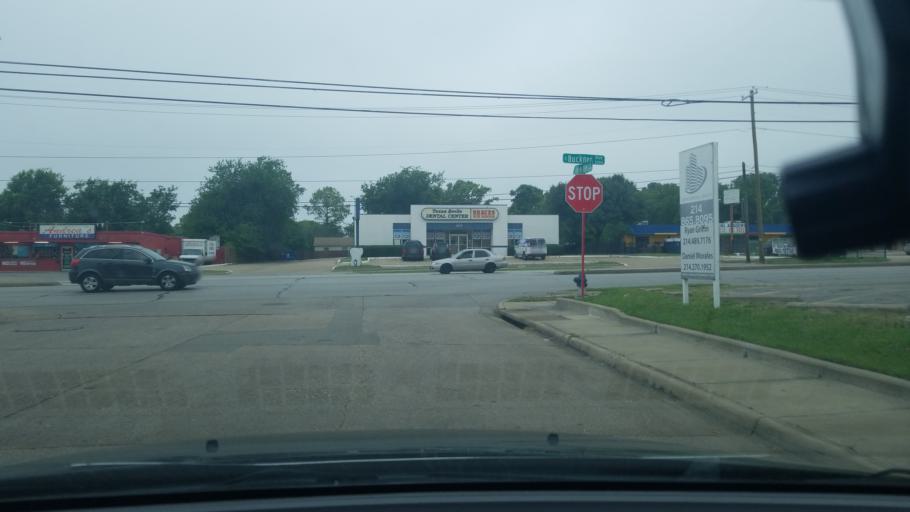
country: US
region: Texas
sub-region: Dallas County
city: Balch Springs
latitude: 32.7551
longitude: -96.6825
